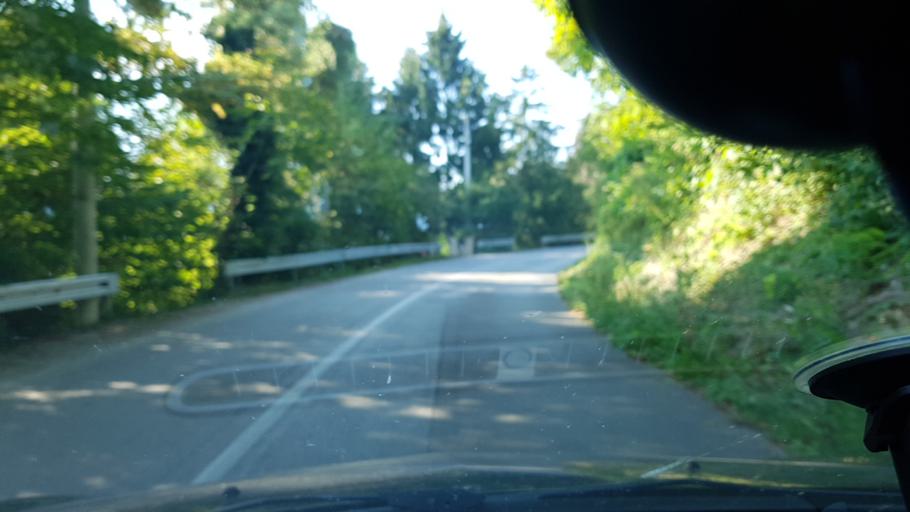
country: HR
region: Zagrebacka
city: Bregana
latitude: 45.8952
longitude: 15.6846
